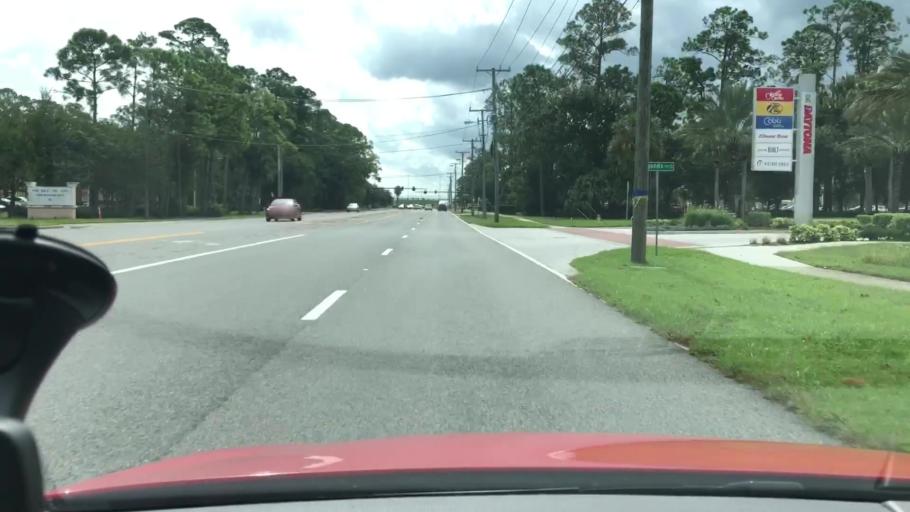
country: US
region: Florida
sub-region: Volusia County
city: Daytona Beach
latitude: 29.1975
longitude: -81.0693
